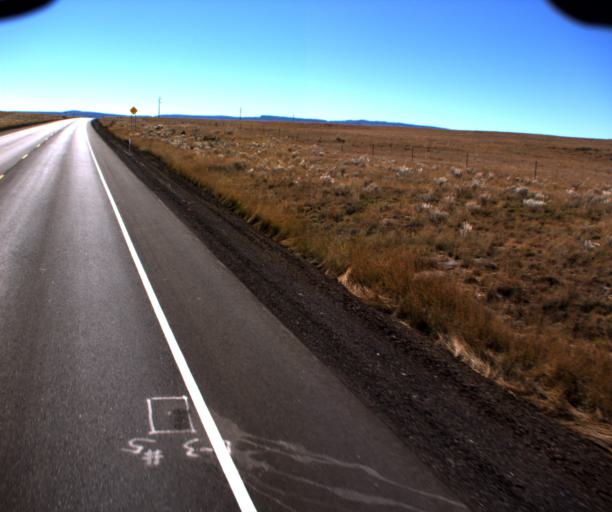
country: US
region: Arizona
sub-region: Apache County
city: Springerville
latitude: 34.1877
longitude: -109.3202
